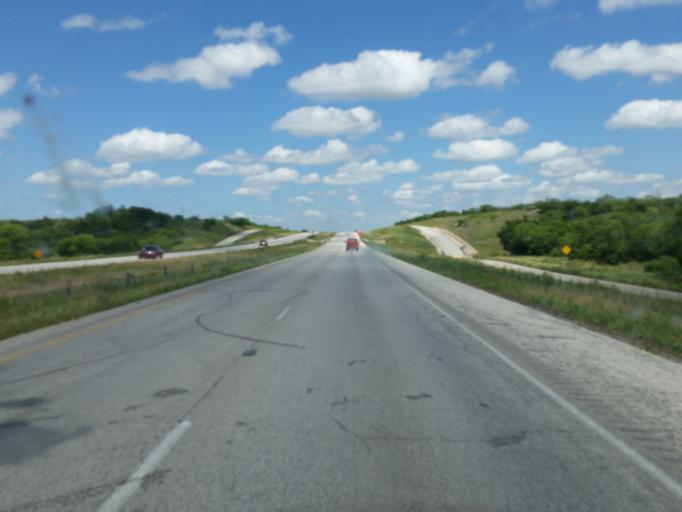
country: US
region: Texas
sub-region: Callahan County
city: Baird
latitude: 32.3814
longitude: -99.2727
